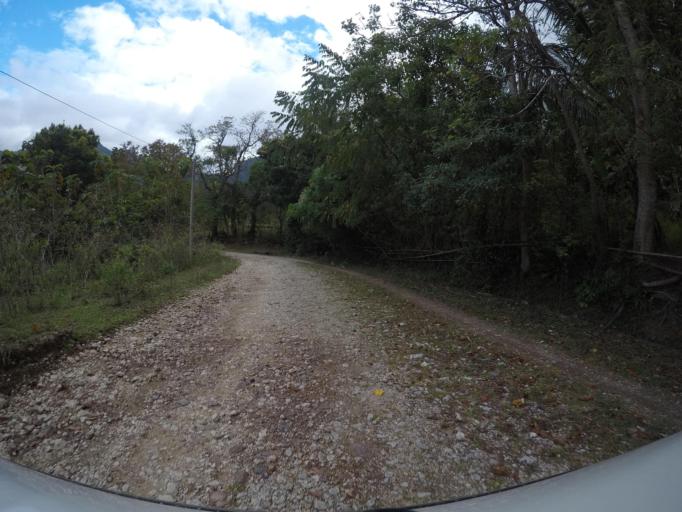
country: TL
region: Baucau
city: Venilale
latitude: -8.6745
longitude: 126.6332
